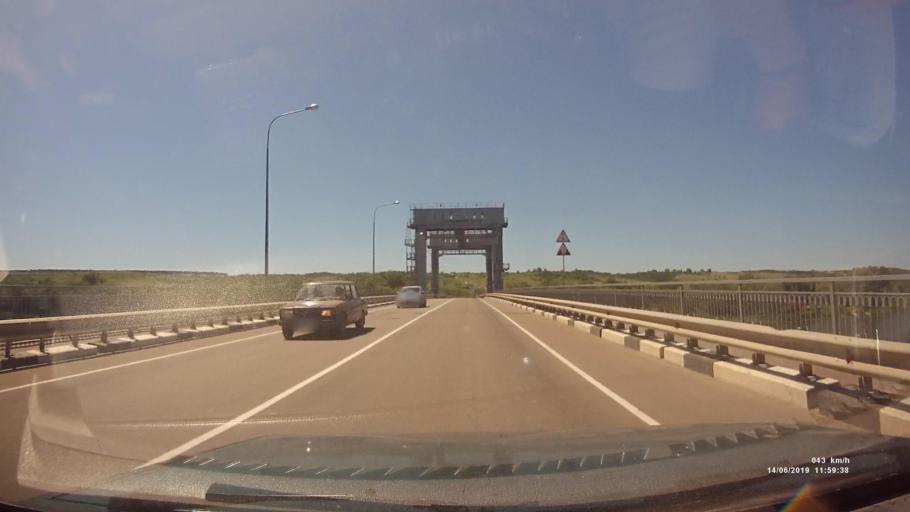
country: RU
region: Rostov
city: Kazanskaya
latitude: 49.7918
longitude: 41.1351
